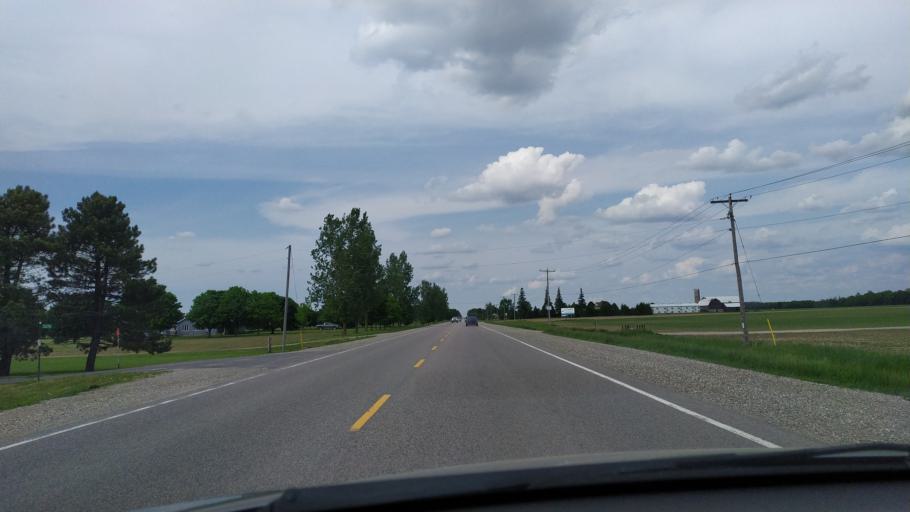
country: CA
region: Ontario
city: Stratford
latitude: 43.3139
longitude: -81.0312
